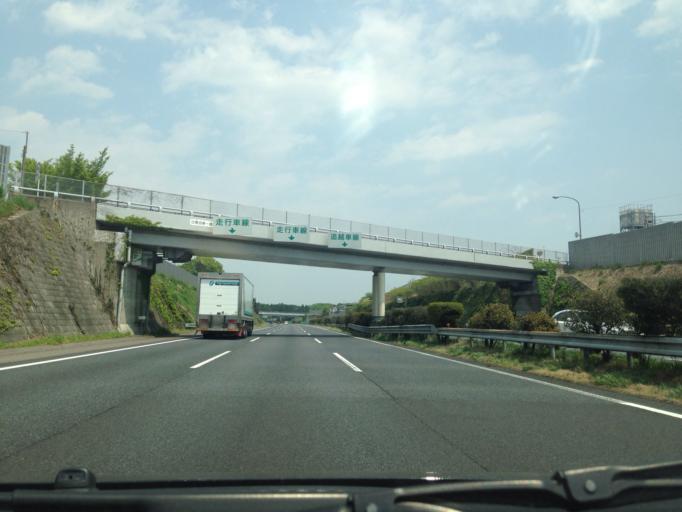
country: JP
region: Tochigi
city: Kanuma
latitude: 36.5526
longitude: 139.8081
